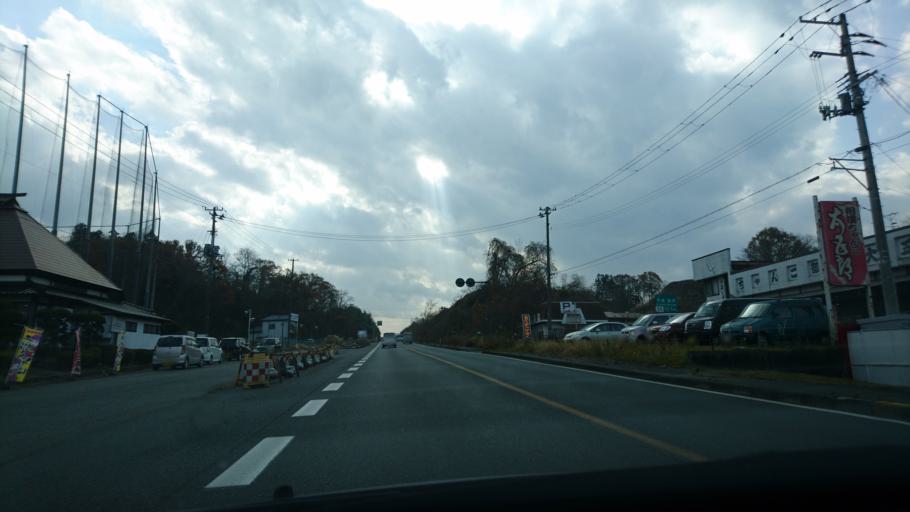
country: JP
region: Iwate
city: Mizusawa
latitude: 39.0316
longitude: 141.1176
